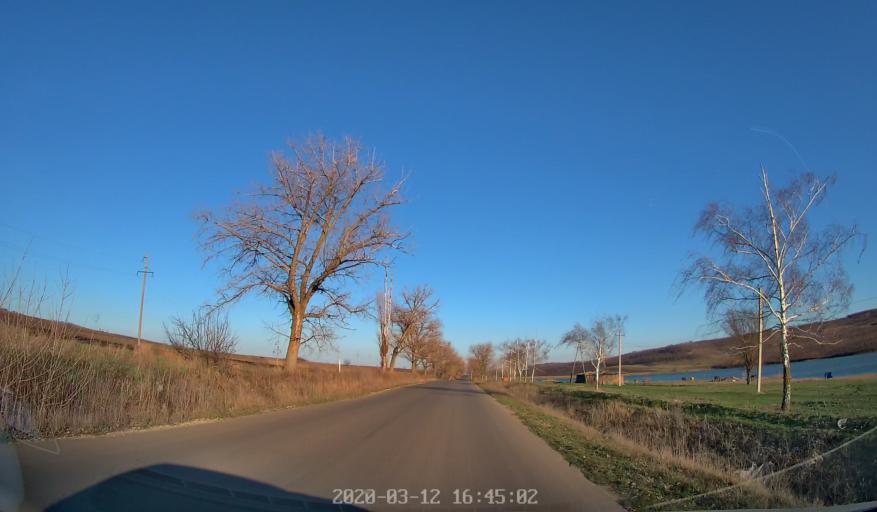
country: MD
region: Anenii Noi
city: Anenii Noi
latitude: 46.8154
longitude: 29.1630
